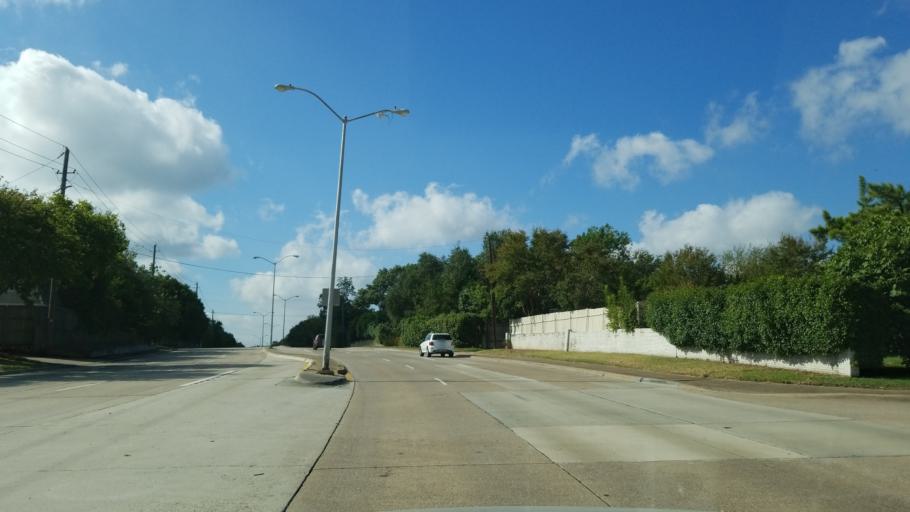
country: US
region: Texas
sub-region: Dallas County
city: Addison
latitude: 32.9486
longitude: -96.7854
